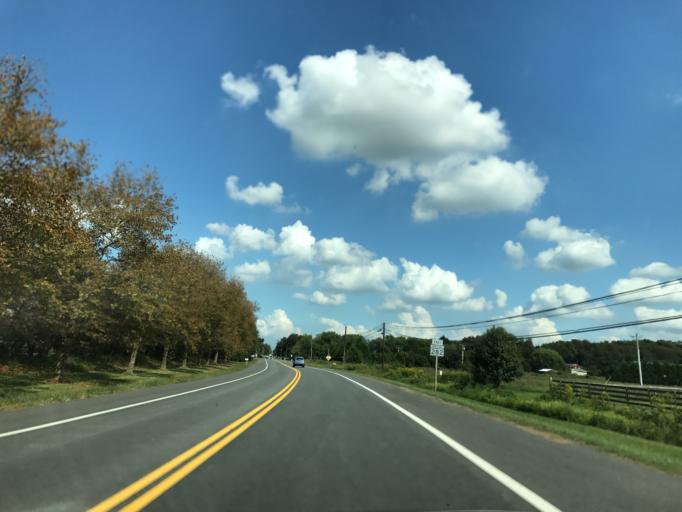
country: US
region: Delaware
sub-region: New Castle County
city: Middletown
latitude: 39.4132
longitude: -75.7834
